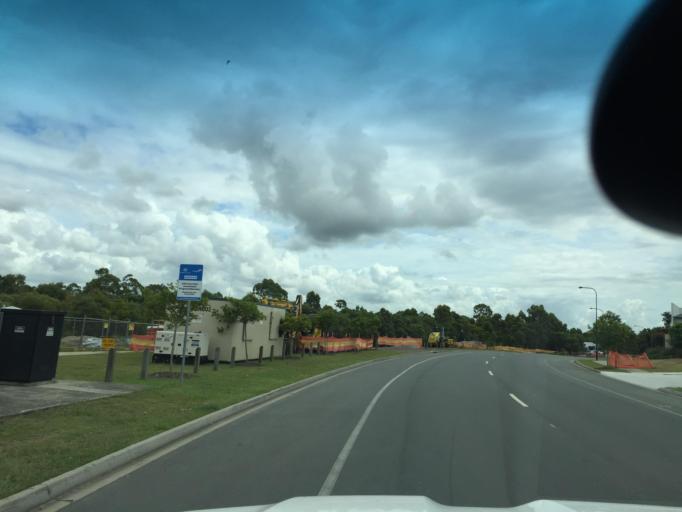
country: AU
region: Queensland
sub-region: Moreton Bay
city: Deception Bay
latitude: -27.2165
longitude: 152.9970
